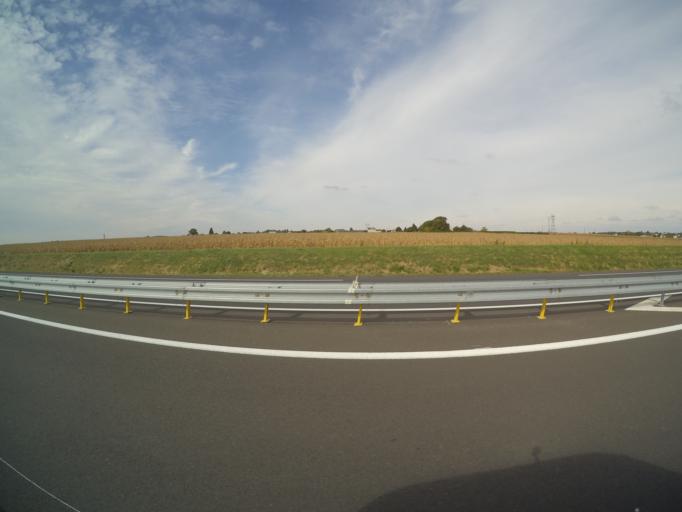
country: FR
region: Pays de la Loire
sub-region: Departement de Maine-et-Loire
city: Distre
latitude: 47.2122
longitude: -0.1830
